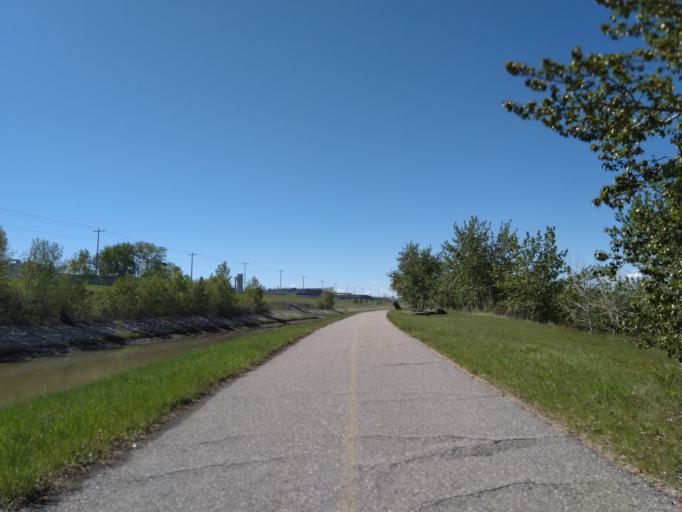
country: CA
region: Alberta
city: Calgary
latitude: 50.9917
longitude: -113.9863
